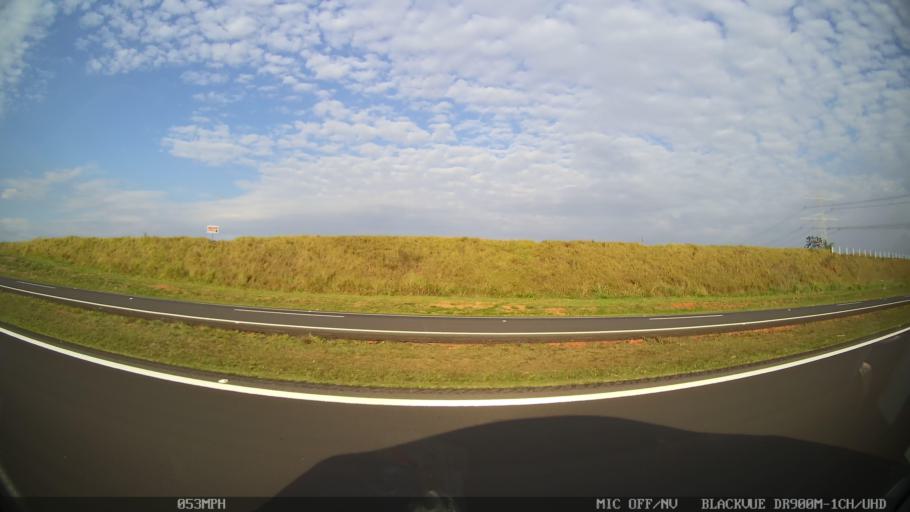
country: BR
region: Sao Paulo
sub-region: Artur Nogueira
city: Artur Nogueira
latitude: -22.6061
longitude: -47.1920
